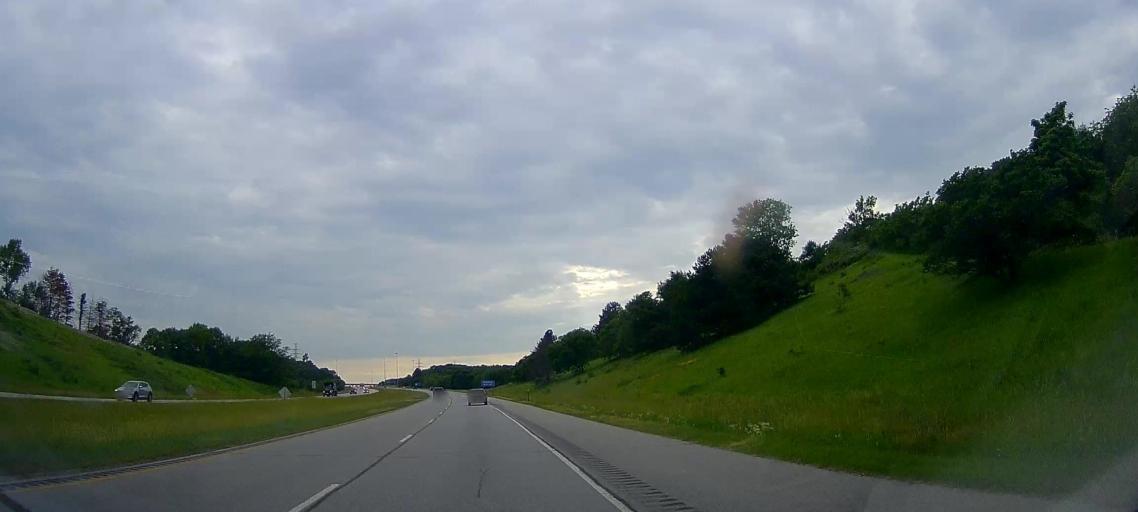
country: US
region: Iowa
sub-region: Pottawattamie County
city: Carter Lake
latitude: 41.3458
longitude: -96.0096
